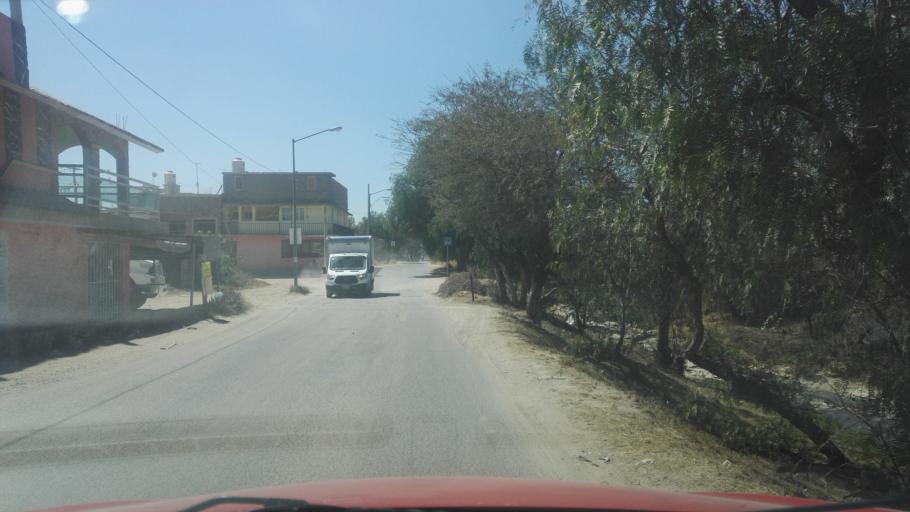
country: MX
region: Guanajuato
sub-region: Leon
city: Fraccionamiento Paraiso Real
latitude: 21.0823
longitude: -101.5955
